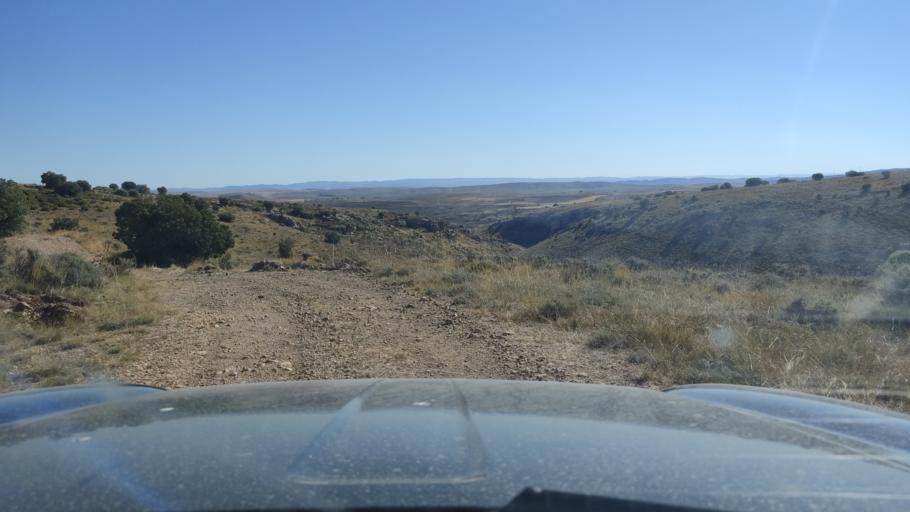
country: ES
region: Aragon
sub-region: Provincia de Teruel
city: Monforte de Moyuela
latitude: 41.0257
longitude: -1.0055
